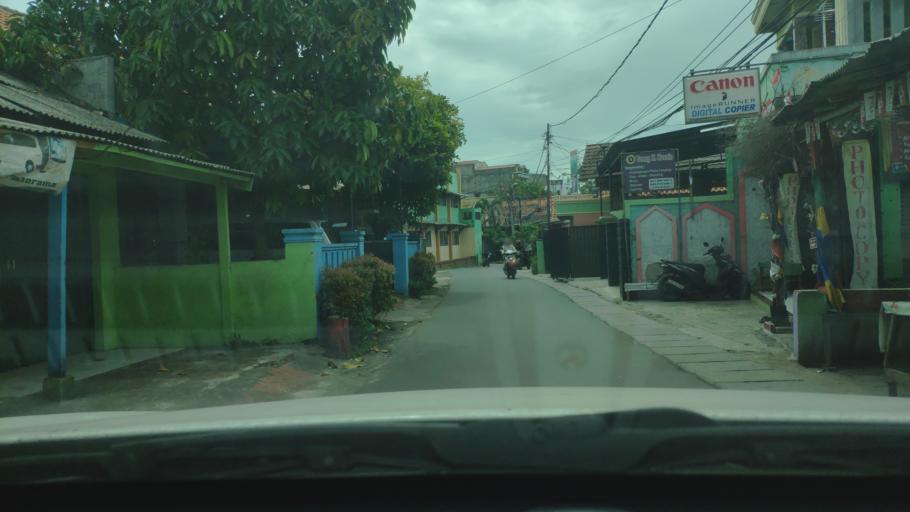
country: ID
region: West Java
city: Ciputat
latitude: -6.2222
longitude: 106.7036
